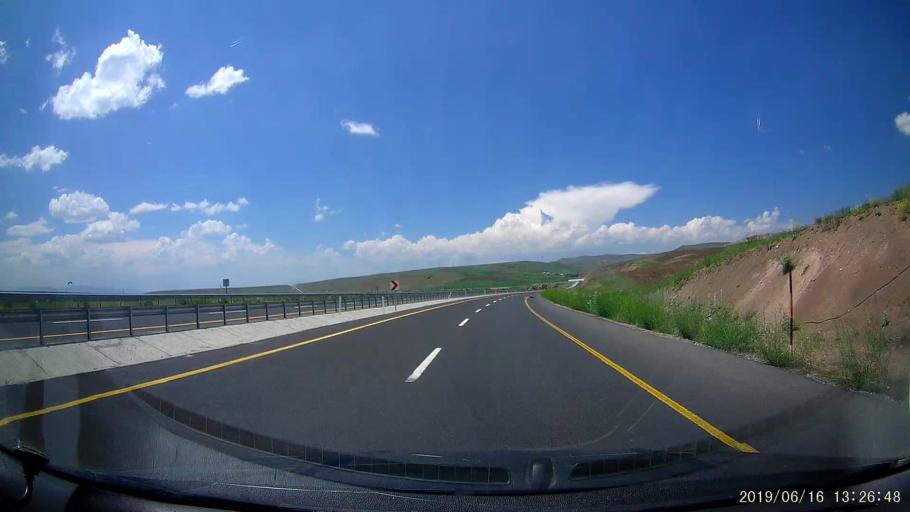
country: TR
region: Agri
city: Taslicay
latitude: 39.6620
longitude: 43.3203
